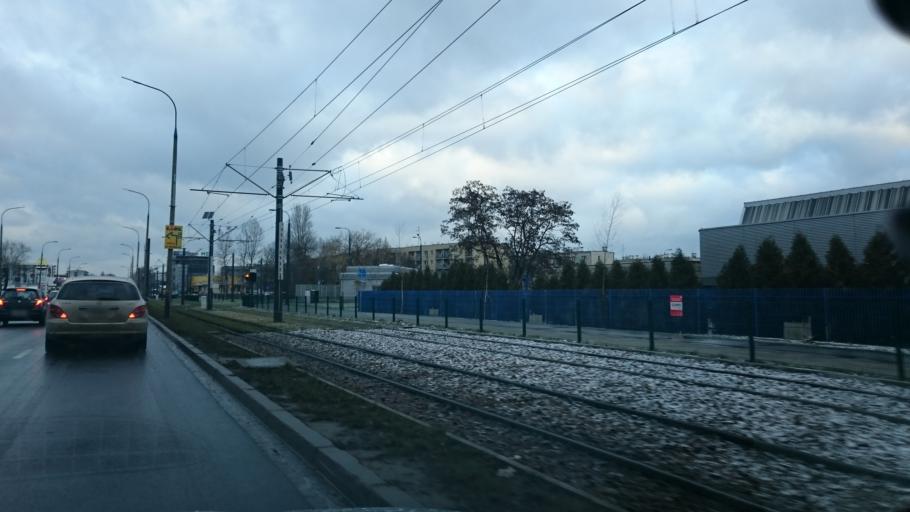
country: PL
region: Lesser Poland Voivodeship
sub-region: Krakow
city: Krakow
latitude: 50.0303
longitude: 19.9734
